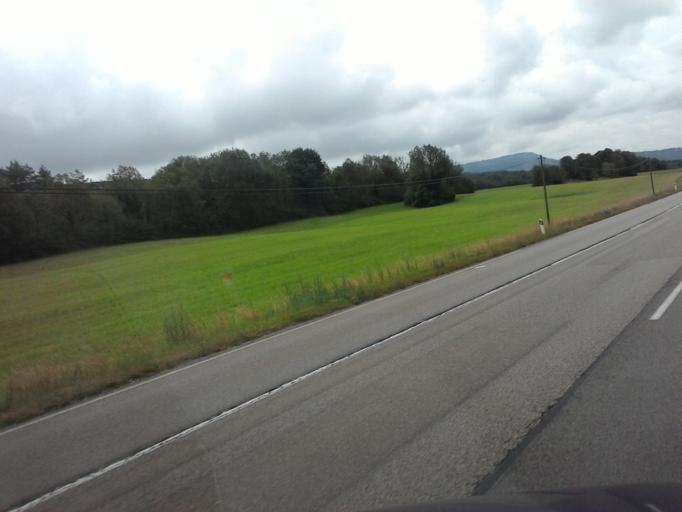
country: FR
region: Franche-Comte
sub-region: Departement du Doubs
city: Quingey
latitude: 47.0286
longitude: 5.8706
